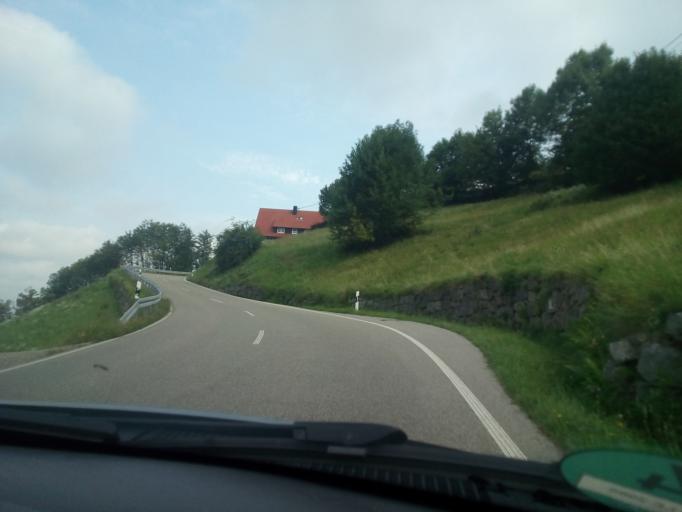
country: DE
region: Baden-Wuerttemberg
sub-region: Freiburg Region
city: Sasbachwalden
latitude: 48.6109
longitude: 8.1389
